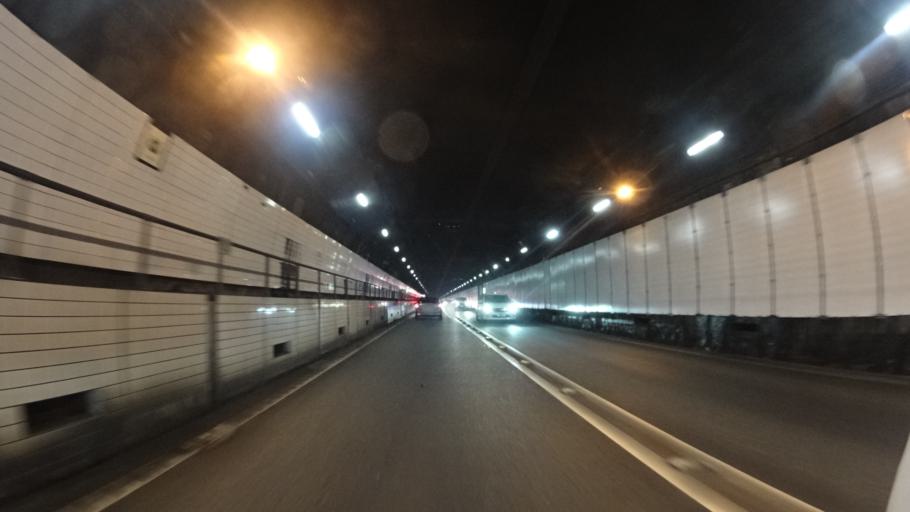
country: JP
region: Yamaguchi
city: Shimonoseki
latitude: 33.9743
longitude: 130.9480
